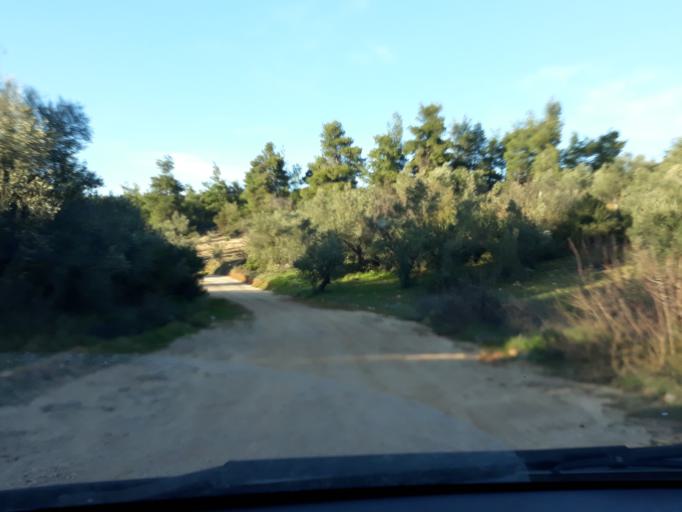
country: GR
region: Central Greece
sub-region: Nomos Voiotias
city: Asopia
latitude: 38.2636
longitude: 23.5353
